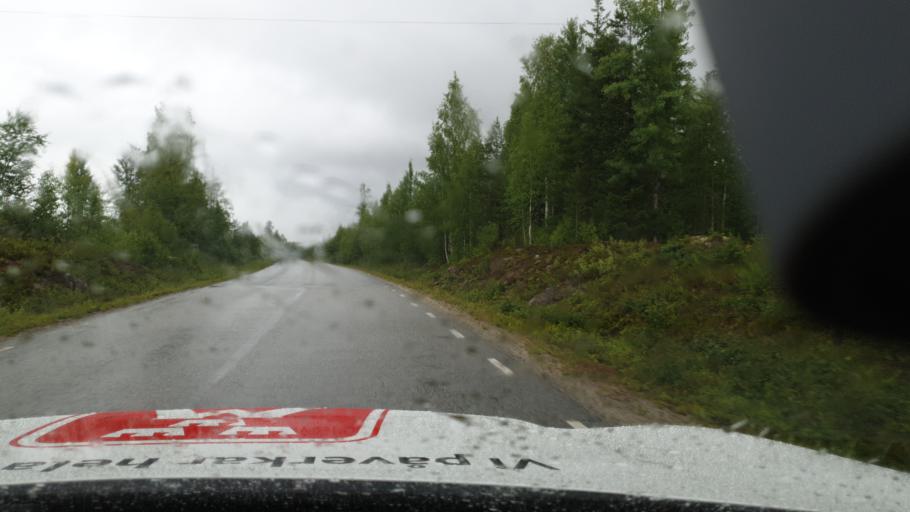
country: SE
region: Vaesterbotten
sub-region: Vindelns Kommun
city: Vindeln
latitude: 64.3172
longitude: 19.6262
